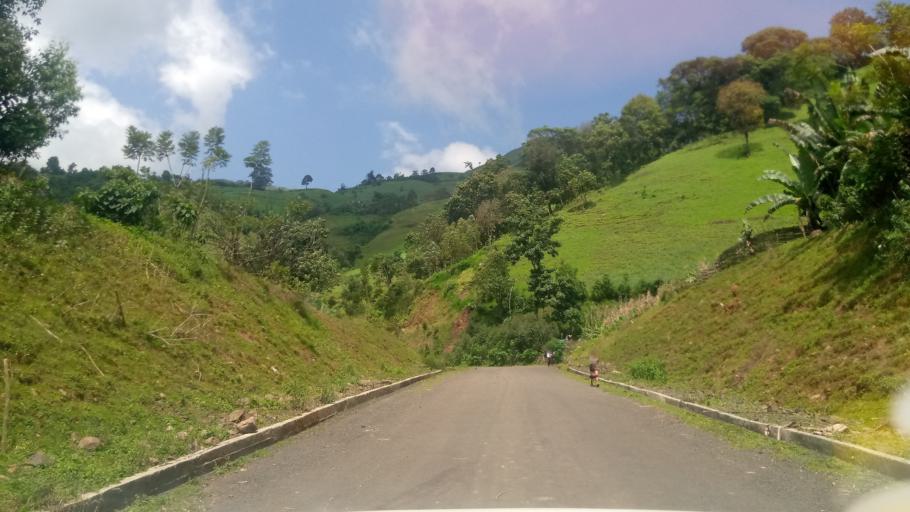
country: ET
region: Southern Nations, Nationalities, and People's Region
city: Bonga
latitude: 7.1463
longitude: 36.5731
